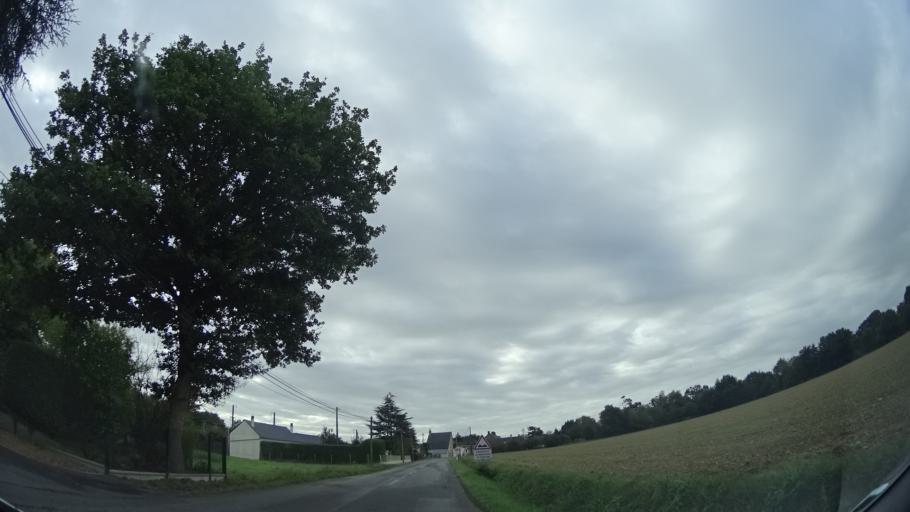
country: FR
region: Brittany
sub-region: Departement d'Ille-et-Vilaine
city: Dinge
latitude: 48.3521
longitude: -1.6880
